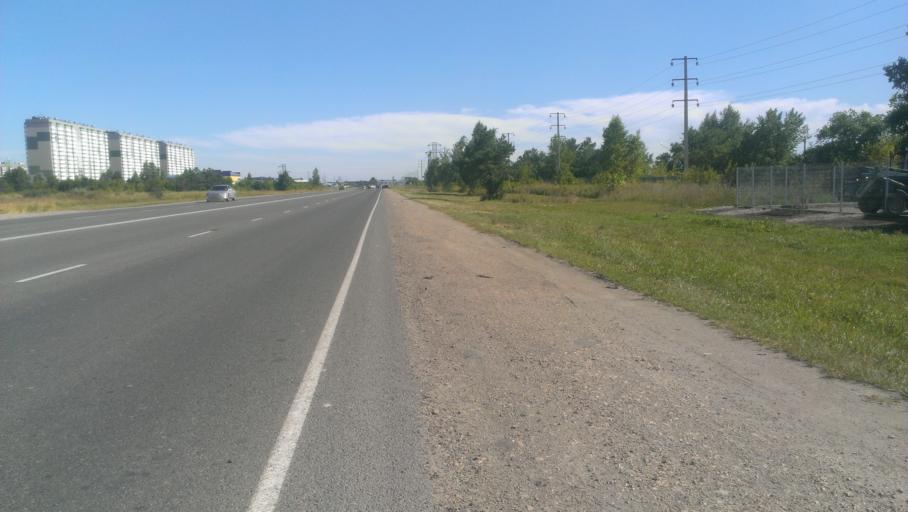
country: RU
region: Altai Krai
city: Novosilikatnyy
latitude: 53.3394
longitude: 83.6401
